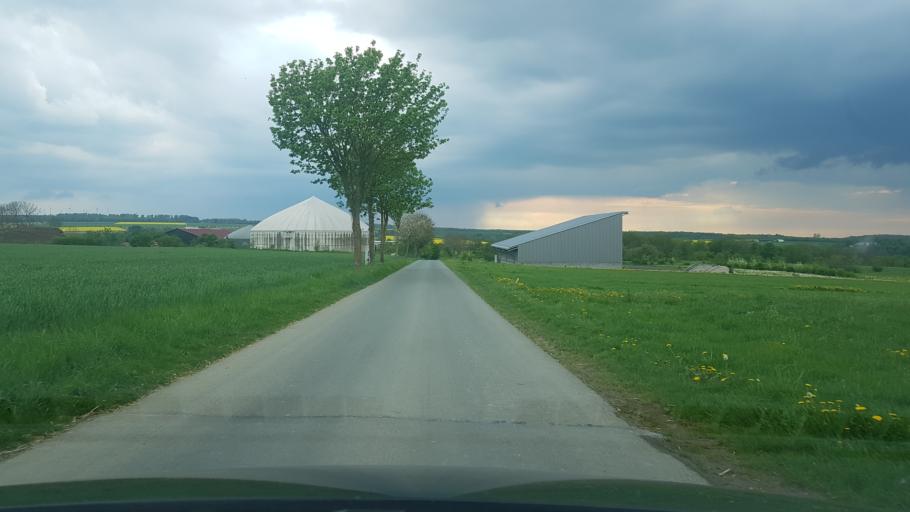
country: DE
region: North Rhine-Westphalia
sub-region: Regierungsbezirk Detmold
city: Paderborn
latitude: 51.6271
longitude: 8.7750
